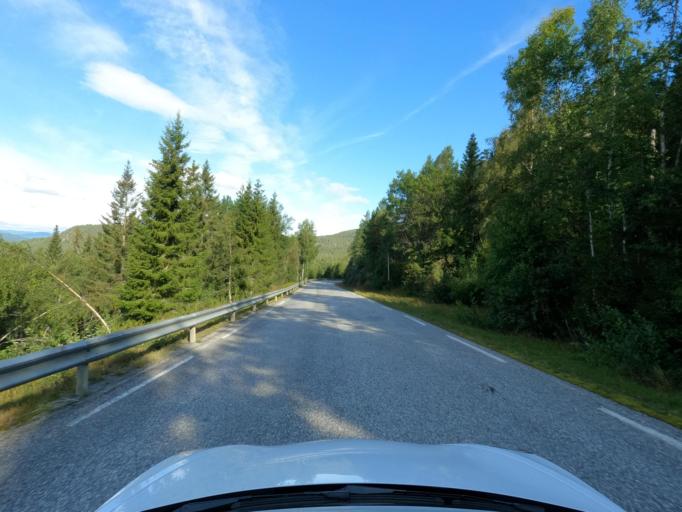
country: NO
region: Telemark
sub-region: Hjartdal
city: Sauland
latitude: 59.9195
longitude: 8.9786
